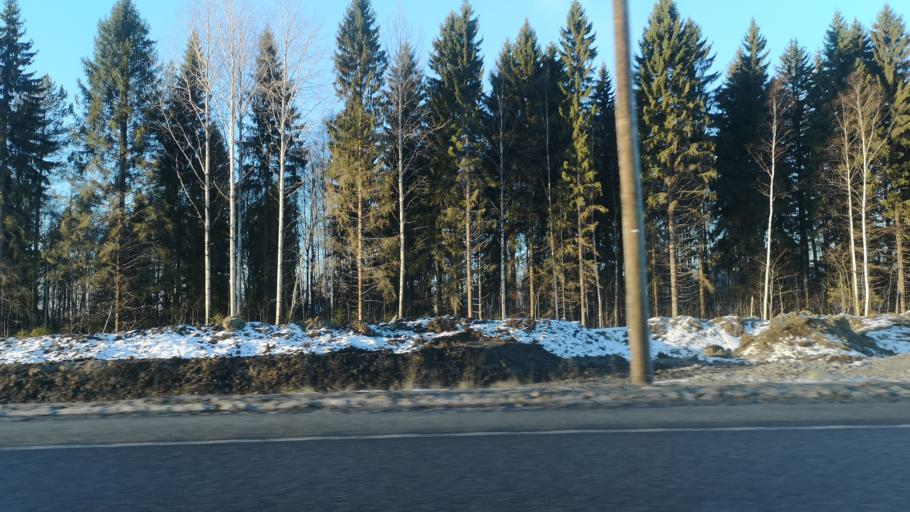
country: FI
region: Southern Savonia
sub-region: Mikkeli
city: Mikkeli
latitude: 61.6976
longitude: 27.3100
